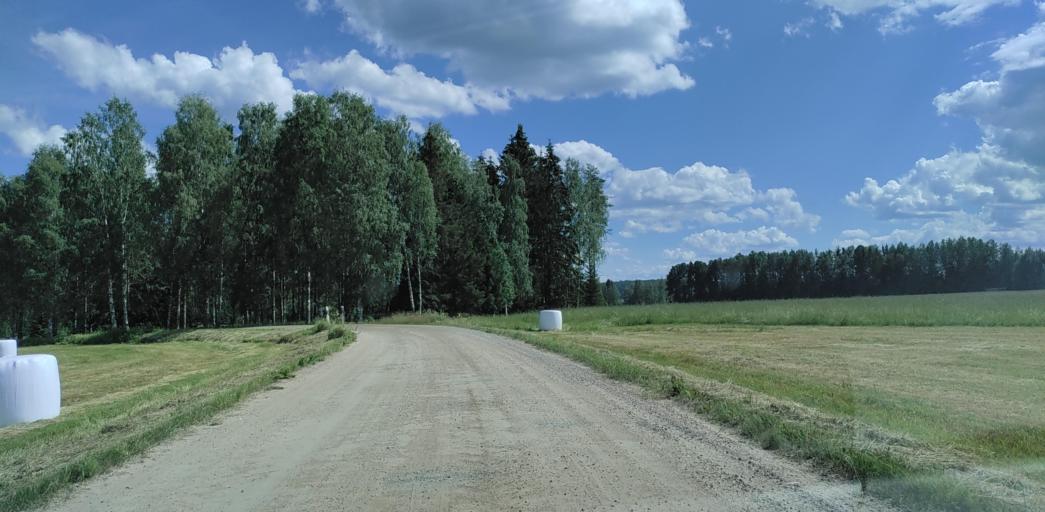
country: SE
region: Vaermland
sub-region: Hagfors Kommun
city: Ekshaerad
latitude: 60.1222
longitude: 13.4826
